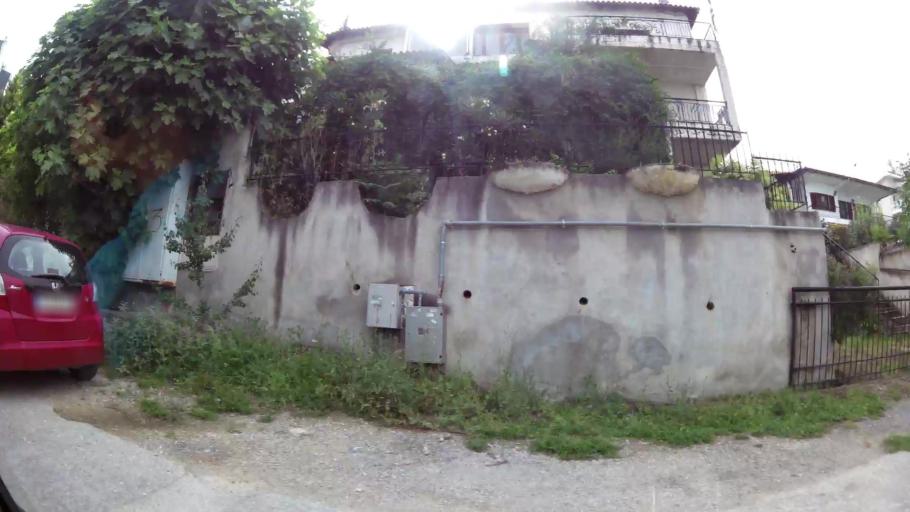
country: GR
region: Central Macedonia
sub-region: Nomos Thessalonikis
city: Panorama
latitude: 40.5859
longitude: 23.0250
